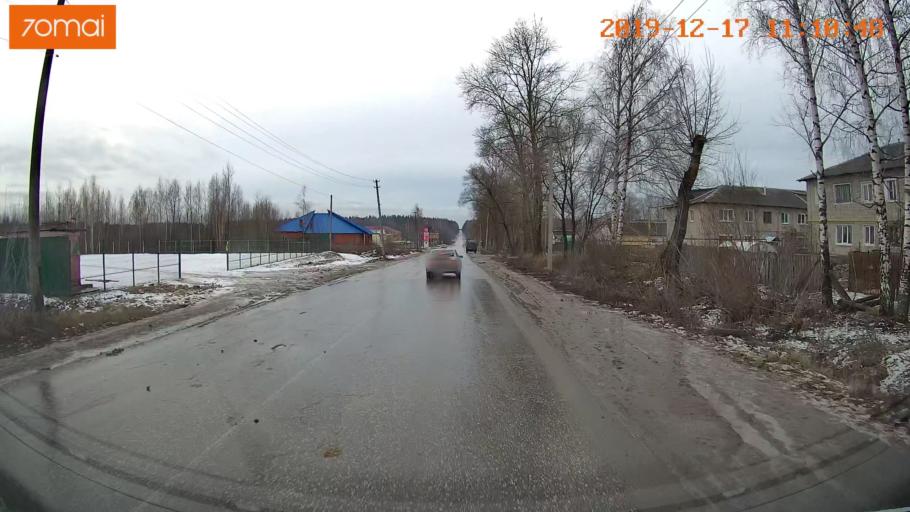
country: RU
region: Vladimir
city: Gus'-Khrustal'nyy
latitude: 55.5903
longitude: 40.6396
